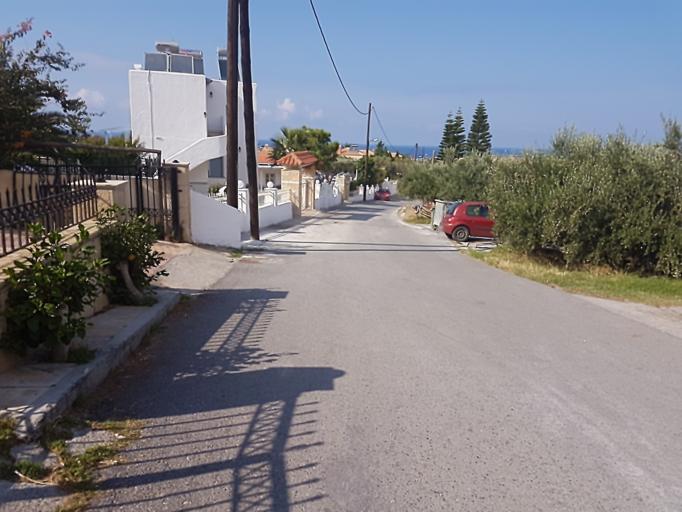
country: GR
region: Crete
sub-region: Nomos Irakleiou
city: Limin Khersonisou
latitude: 35.3153
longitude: 25.3859
